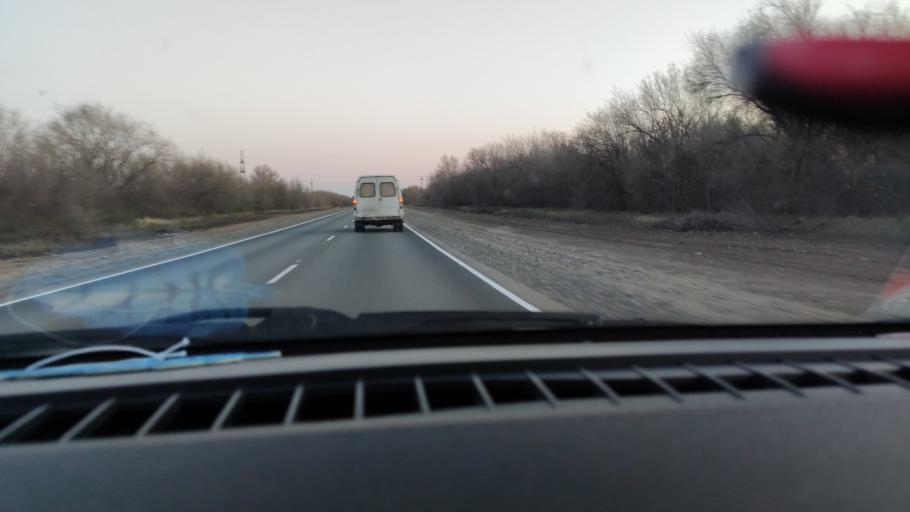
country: RU
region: Saratov
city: Krasnoarmeysk
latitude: 51.1313
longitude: 45.9593
